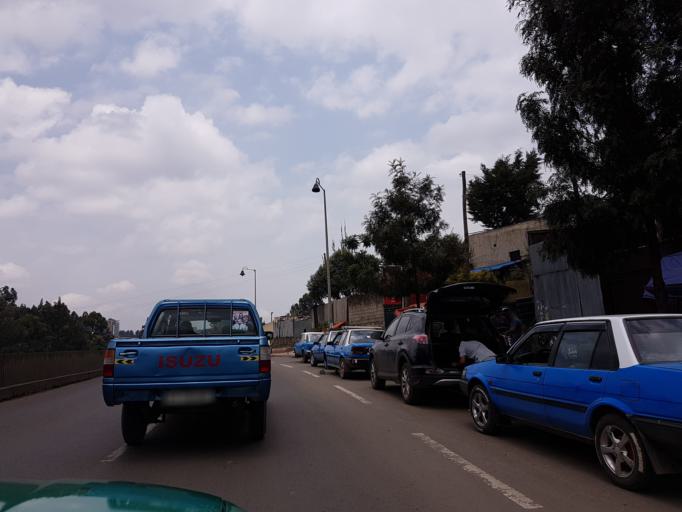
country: ET
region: Adis Abeba
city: Addis Ababa
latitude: 9.0060
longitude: 38.7337
